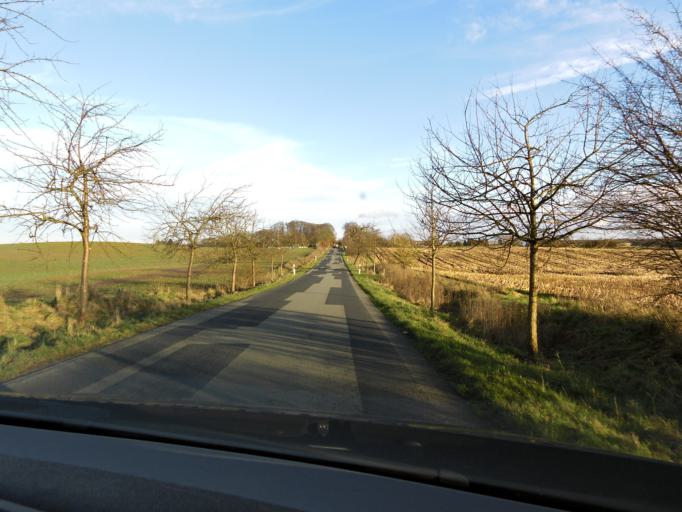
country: DE
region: Mecklenburg-Vorpommern
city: Roggendorf
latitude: 53.6596
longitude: 10.9743
